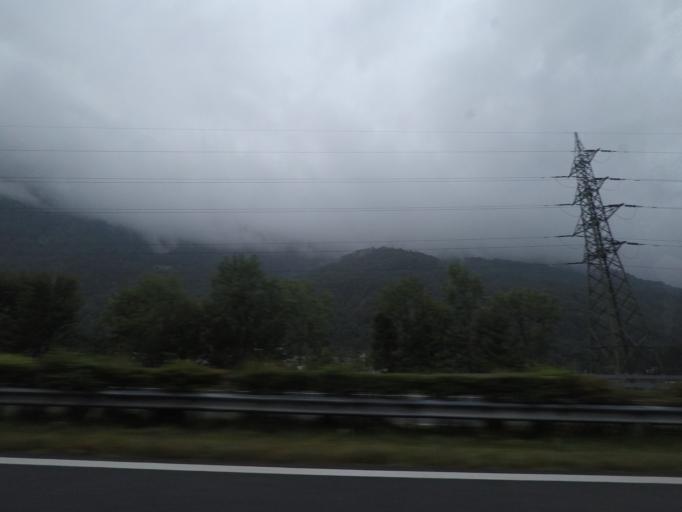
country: CH
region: Valais
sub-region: Martigny District
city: Evionnaz
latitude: 46.1732
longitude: 7.0263
